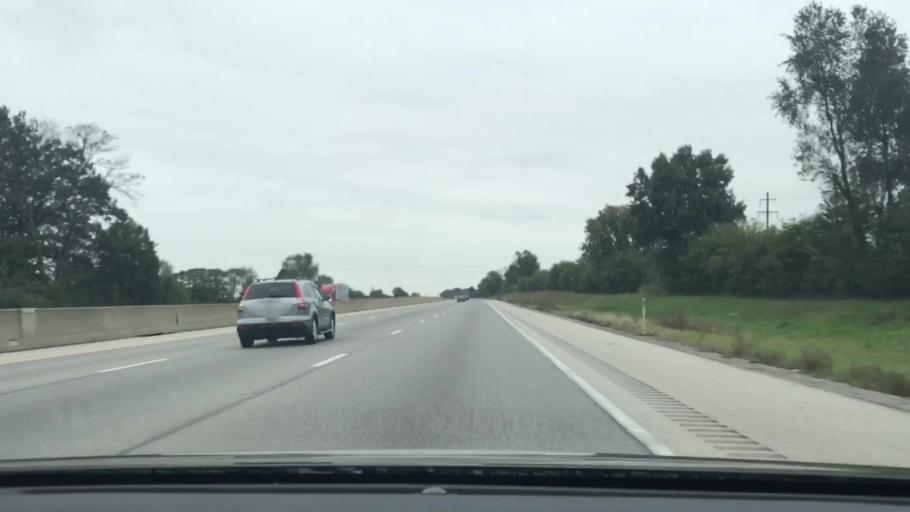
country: US
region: Kentucky
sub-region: Warren County
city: Plano
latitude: 36.8813
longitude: -86.4445
